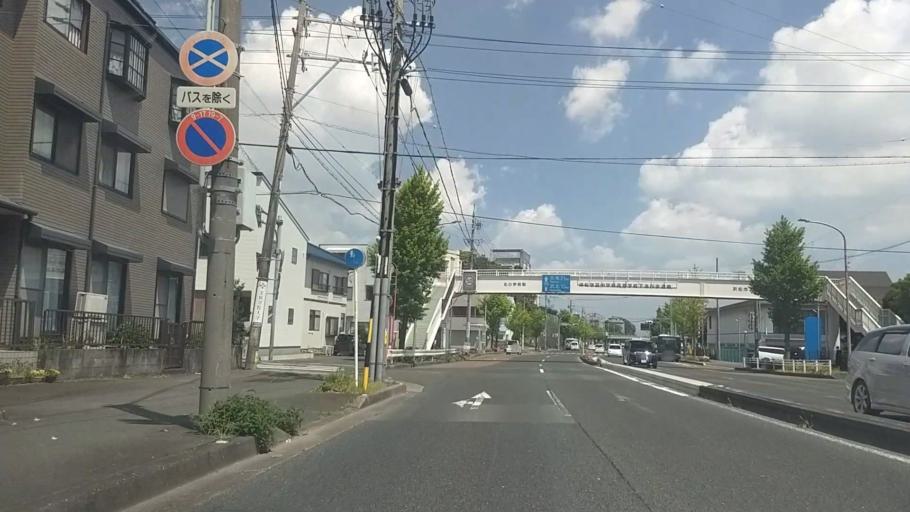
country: JP
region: Shizuoka
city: Hamamatsu
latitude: 34.7173
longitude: 137.7285
